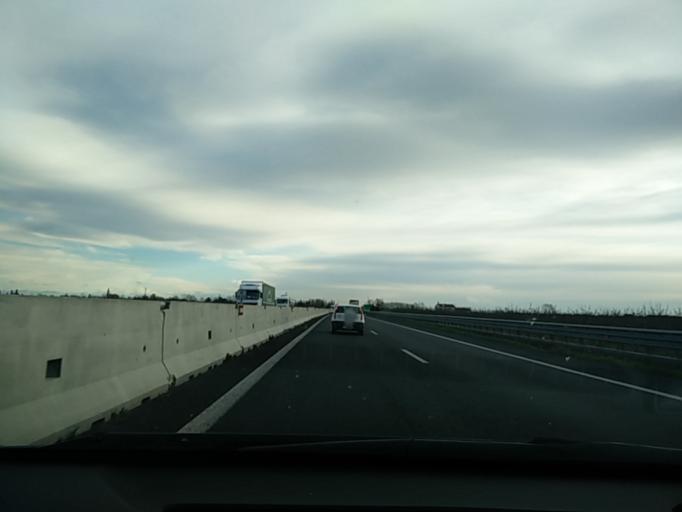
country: IT
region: Veneto
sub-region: Provincia di Treviso
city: Cessalto
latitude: 45.6986
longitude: 12.5889
